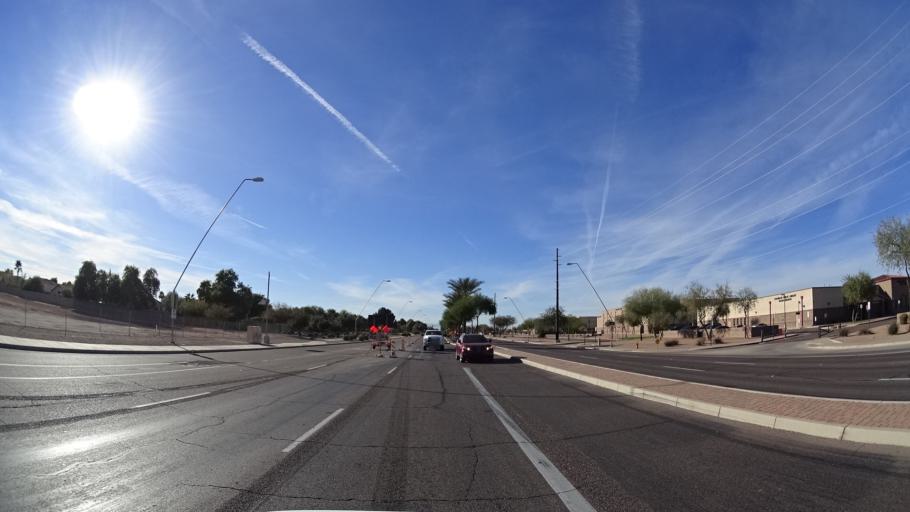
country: US
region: Arizona
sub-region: Maricopa County
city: Sun Lakes
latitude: 33.2192
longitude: -111.7561
